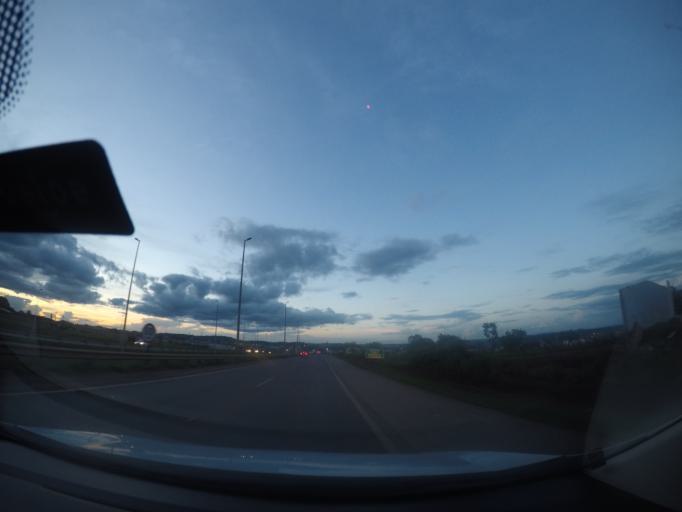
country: BR
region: Goias
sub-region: Goianira
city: Goianira
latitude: -16.5187
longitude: -49.4162
